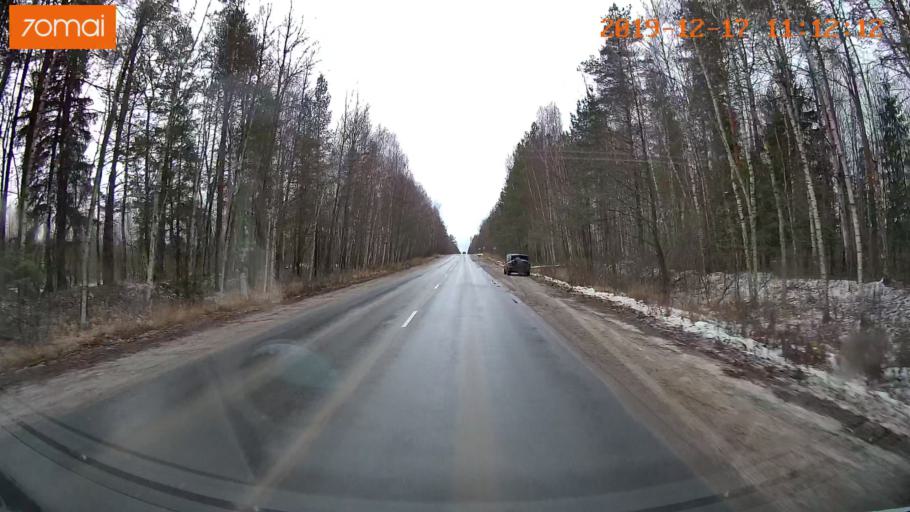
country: RU
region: Vladimir
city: Gus'-Khrustal'nyy
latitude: 55.5788
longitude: 40.6307
